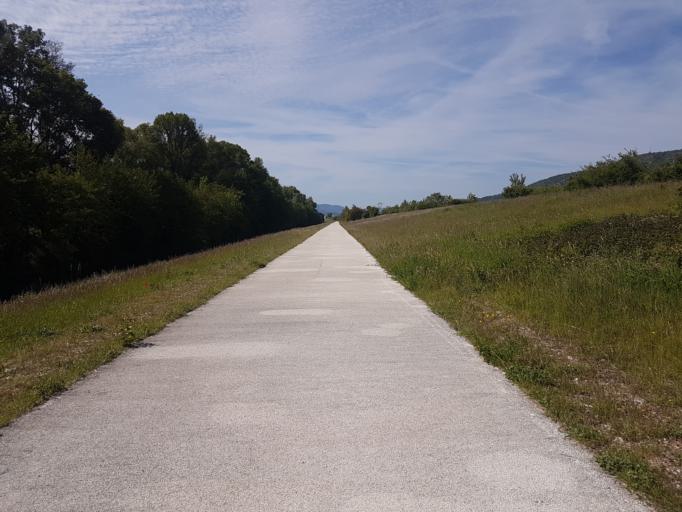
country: FR
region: Rhone-Alpes
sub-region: Departement de l'Ardeche
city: Le Pouzin
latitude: 44.7657
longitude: 4.7588
